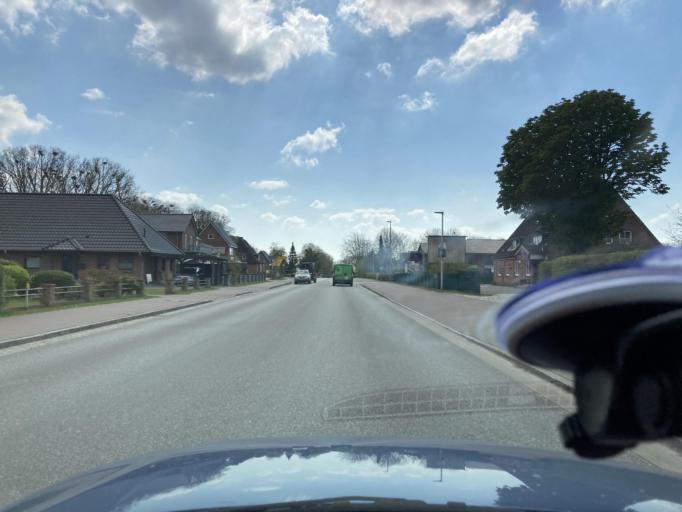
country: DE
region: Schleswig-Holstein
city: Hemmingstedt
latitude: 54.1480
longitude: 9.0726
